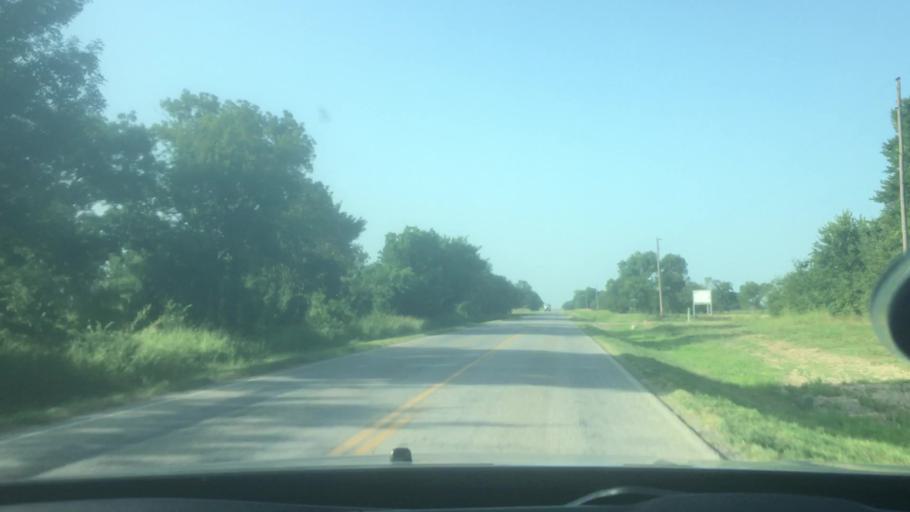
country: US
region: Oklahoma
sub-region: Johnston County
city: Tishomingo
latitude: 34.2963
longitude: -96.4248
